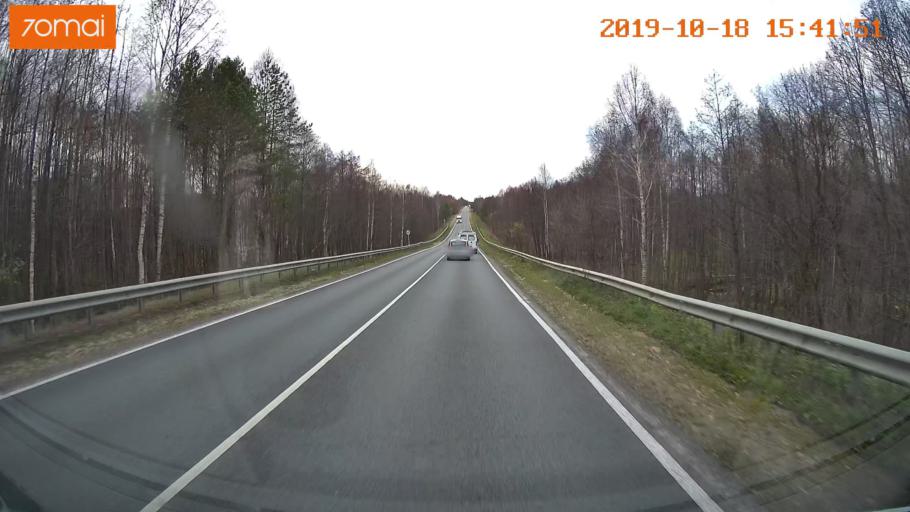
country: RU
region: Vladimir
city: Golovino
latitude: 55.9497
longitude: 40.5769
